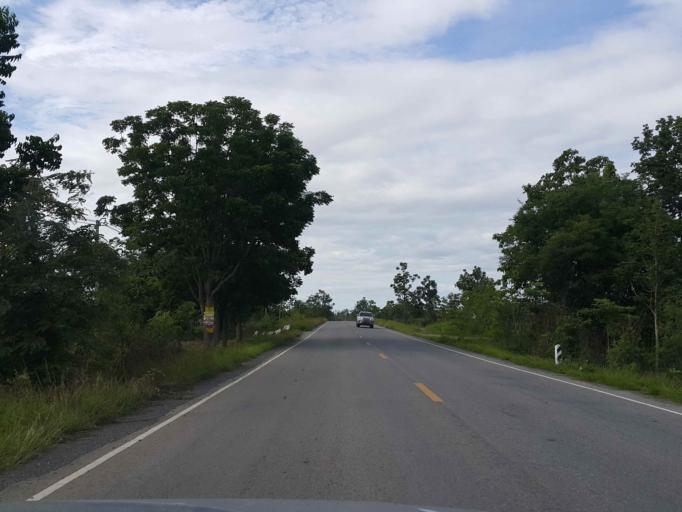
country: TH
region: Sukhothai
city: Thung Saliam
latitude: 17.2402
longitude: 99.5158
